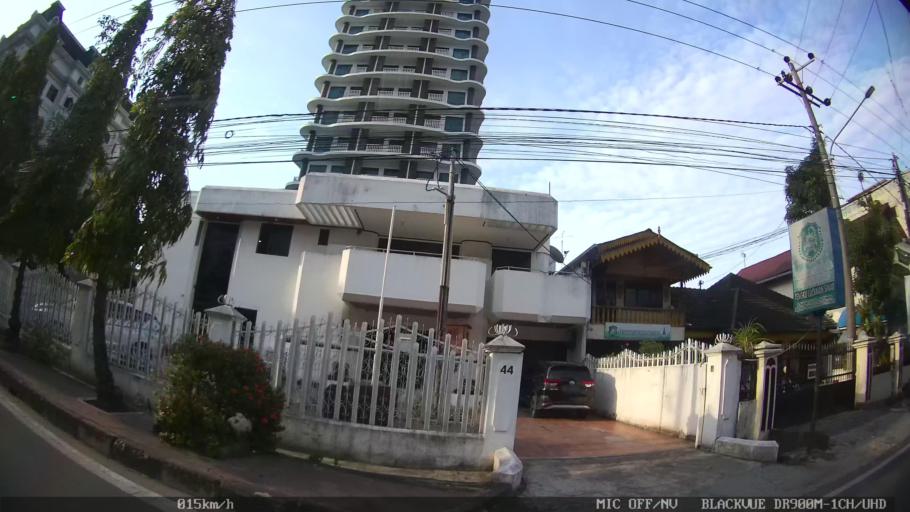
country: ID
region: North Sumatra
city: Medan
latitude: 3.5769
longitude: 98.6576
